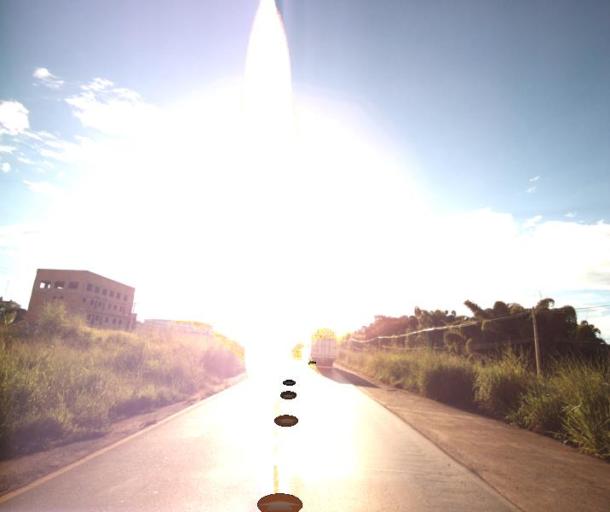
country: BR
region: Goias
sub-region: Anapolis
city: Anapolis
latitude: -16.2852
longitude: -48.9481
